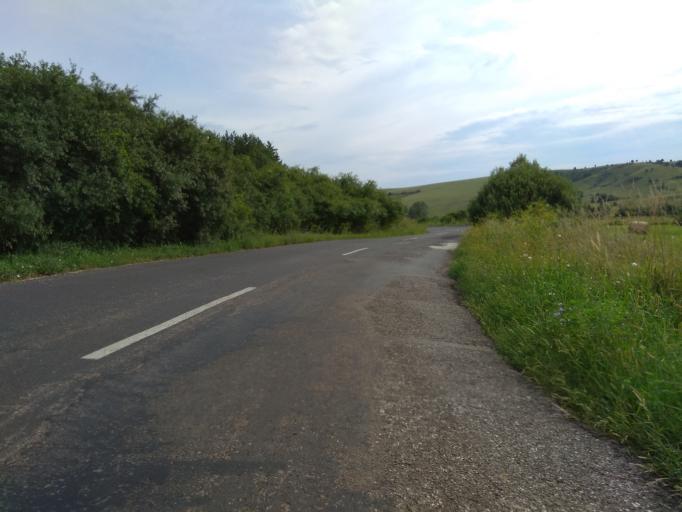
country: HU
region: Heves
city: Tarnalelesz
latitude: 48.0396
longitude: 20.2507
